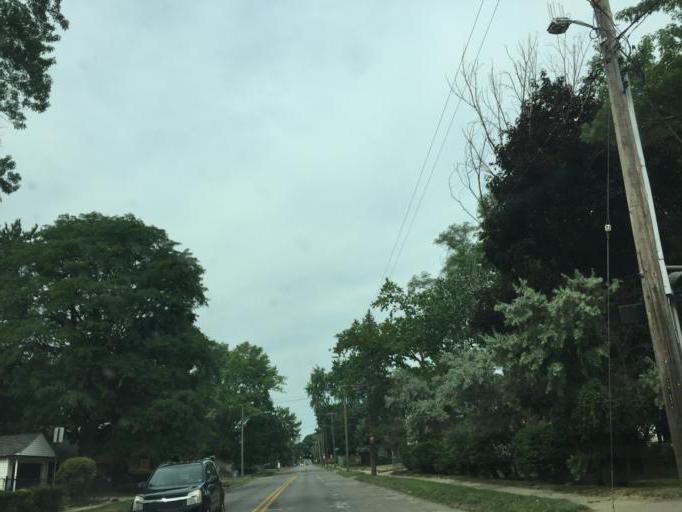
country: US
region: Michigan
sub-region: Wayne County
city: Redford
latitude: 42.4009
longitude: -83.2276
